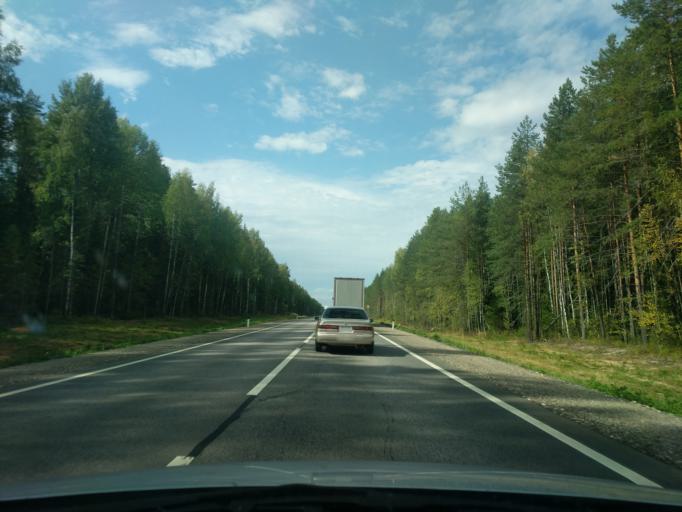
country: RU
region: Kostroma
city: Kadyy
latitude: 57.7970
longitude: 42.8415
